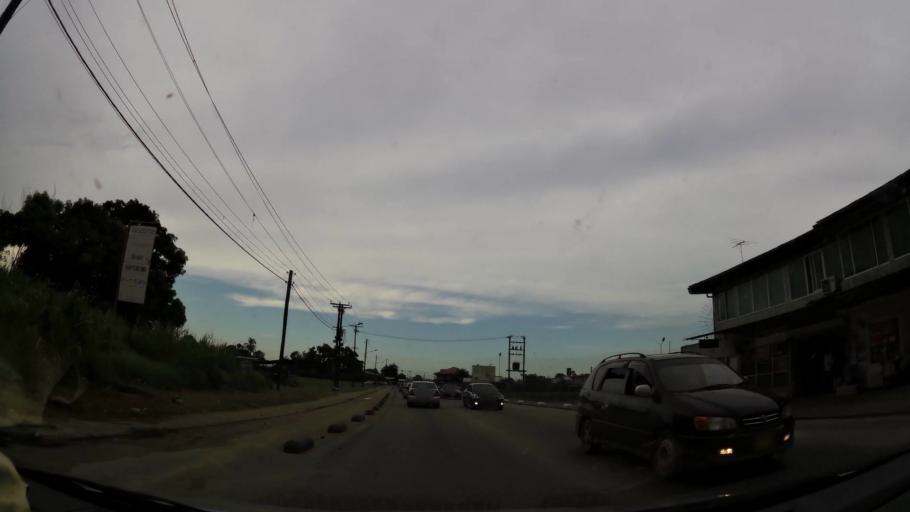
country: SR
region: Paramaribo
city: Paramaribo
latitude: 5.7958
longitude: -55.1899
